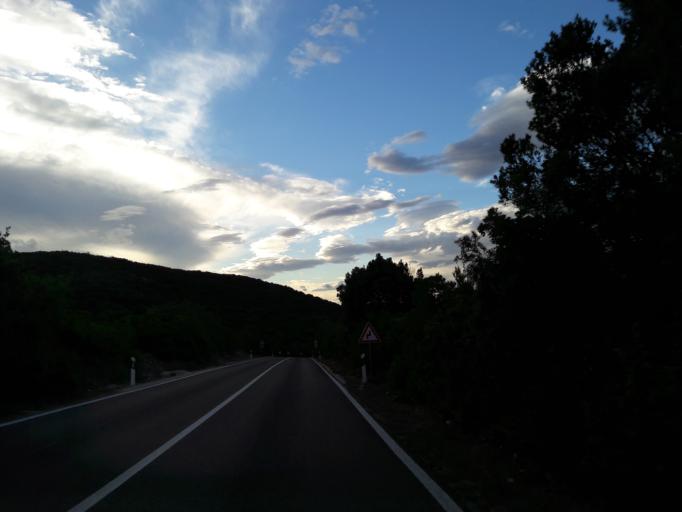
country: HR
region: Dubrovacko-Neretvanska
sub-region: Grad Dubrovnik
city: Opuzen
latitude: 42.9082
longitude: 17.4778
